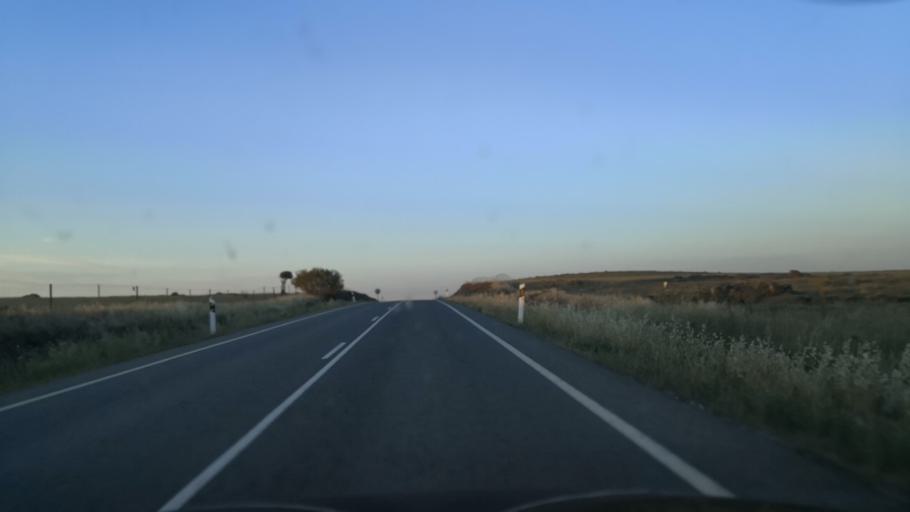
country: ES
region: Extremadura
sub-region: Provincia de Caceres
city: Alcantara
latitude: 39.6666
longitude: -6.8773
